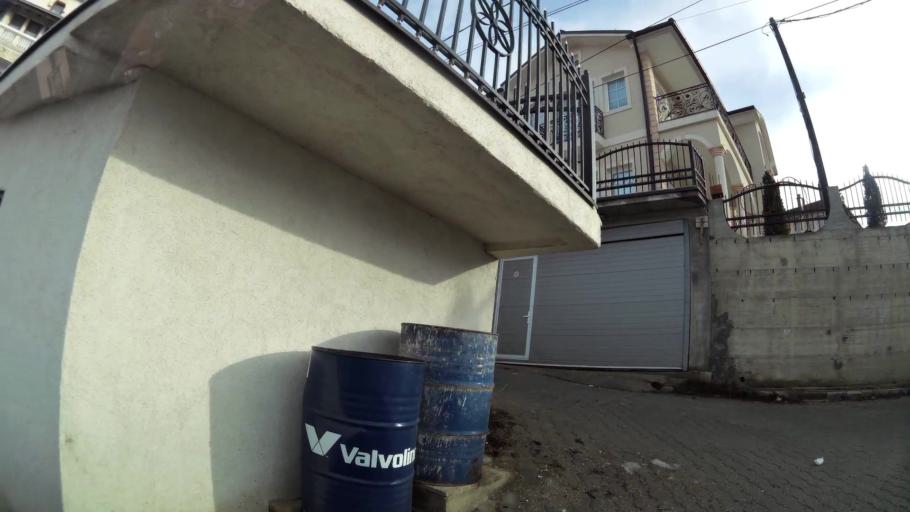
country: XK
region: Pristina
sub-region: Komuna e Prishtines
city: Pristina
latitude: 42.6719
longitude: 21.1770
